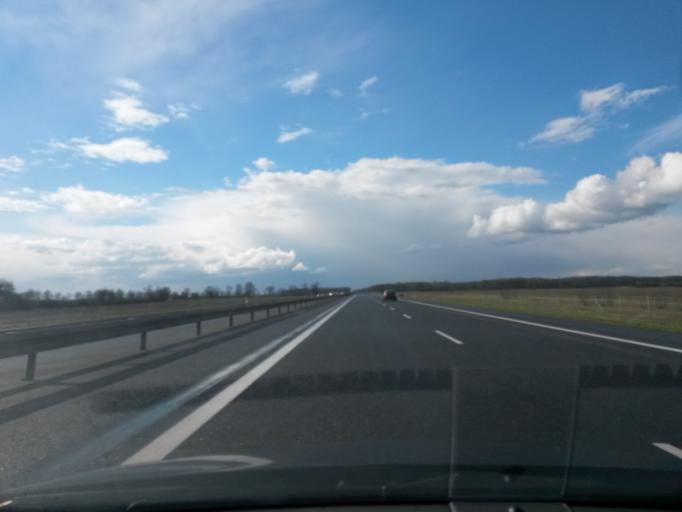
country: PL
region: Greater Poland Voivodeship
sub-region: Powiat wrzesinski
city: Wrzesnia
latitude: 52.2996
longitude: 17.6304
